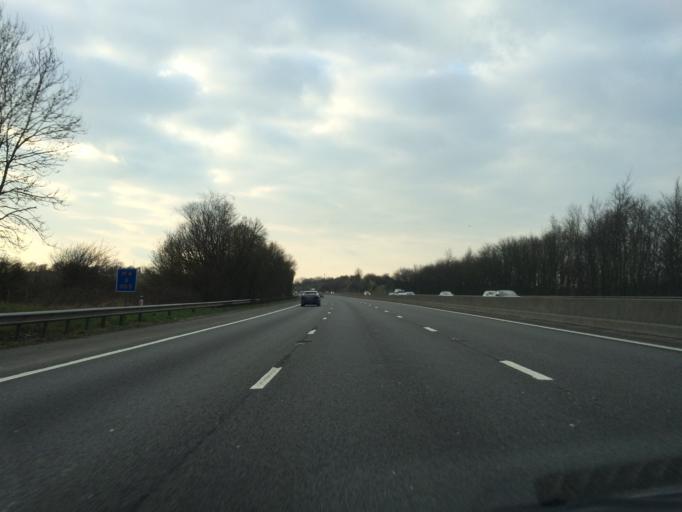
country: GB
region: England
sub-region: Wiltshire
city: Aldbourne
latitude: 51.5021
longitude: -1.5893
